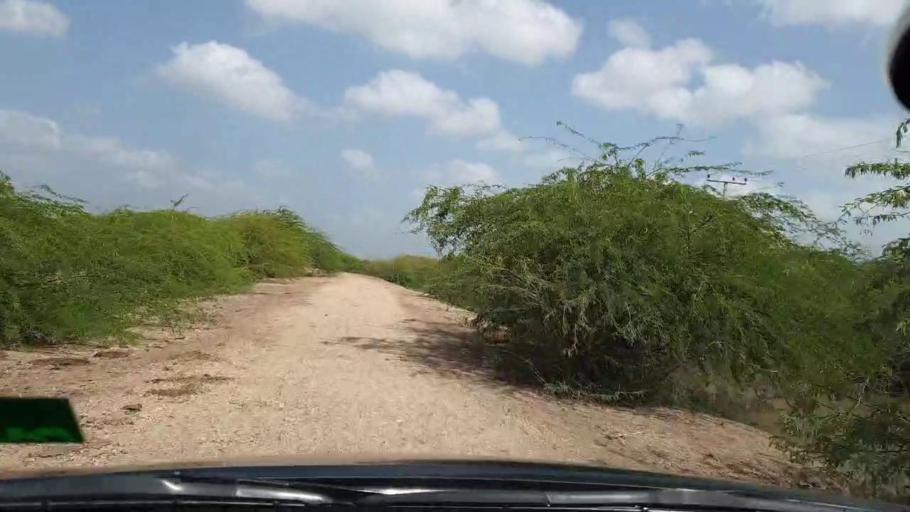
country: PK
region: Sindh
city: Kadhan
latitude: 24.6298
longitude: 69.1450
